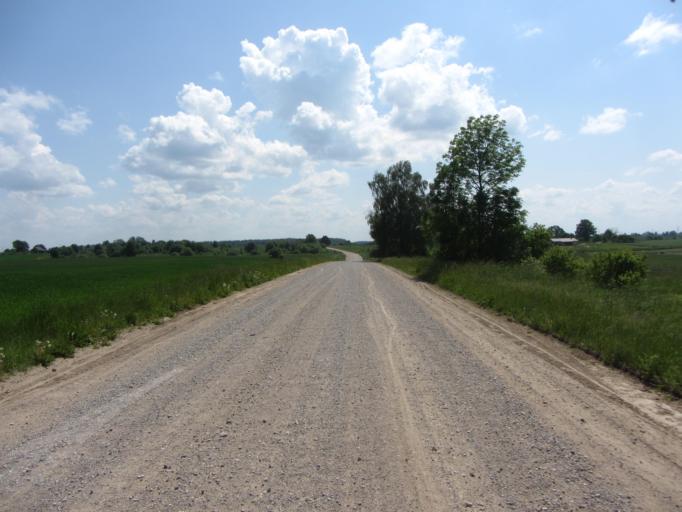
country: LT
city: Kaisiadorys
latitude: 54.8789
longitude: 24.2575
